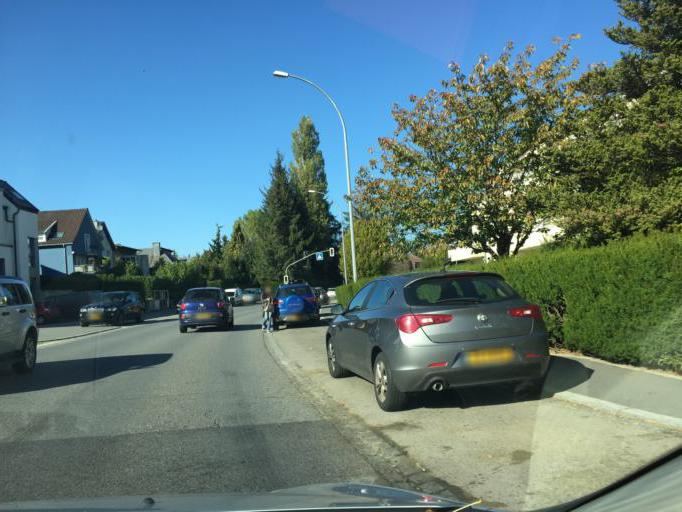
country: LU
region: Luxembourg
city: Bridel
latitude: 49.6506
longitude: 6.0829
